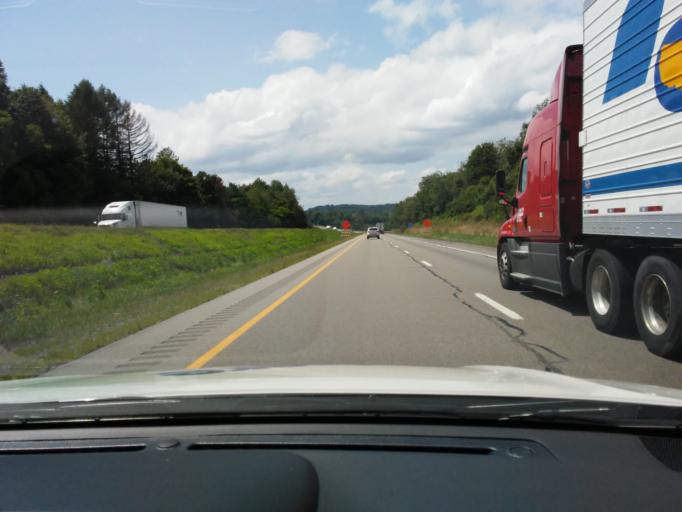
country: US
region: Pennsylvania
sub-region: Jefferson County
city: Brookville
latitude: 41.1858
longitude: -79.1665
